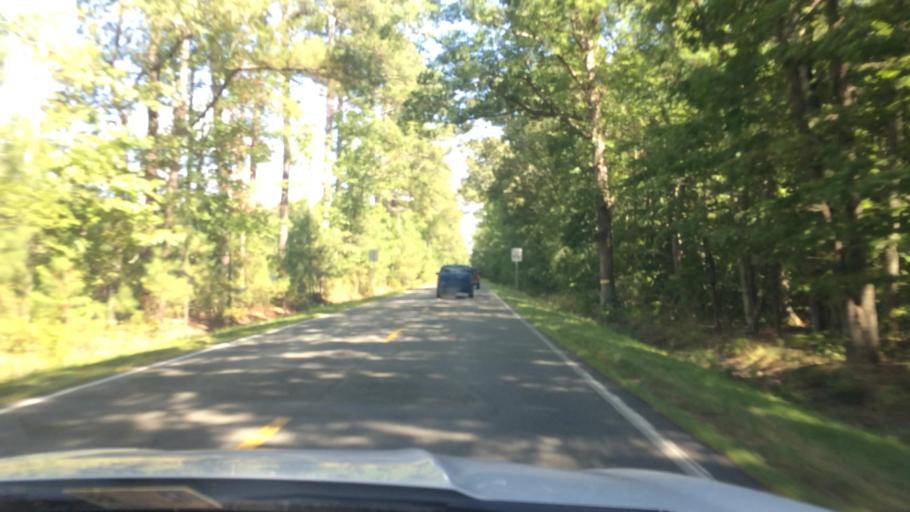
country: US
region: Virginia
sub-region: Surry County
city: Surry
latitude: 37.2745
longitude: -76.9076
